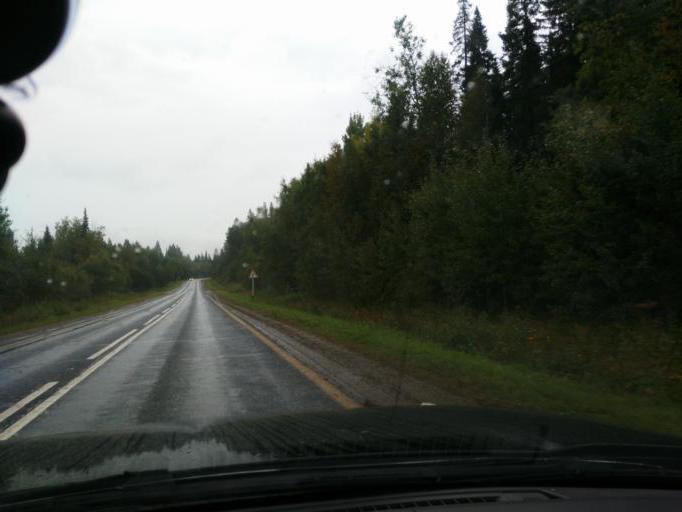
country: RU
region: Perm
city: Yugo-Kamskiy
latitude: 57.5232
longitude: 55.6847
